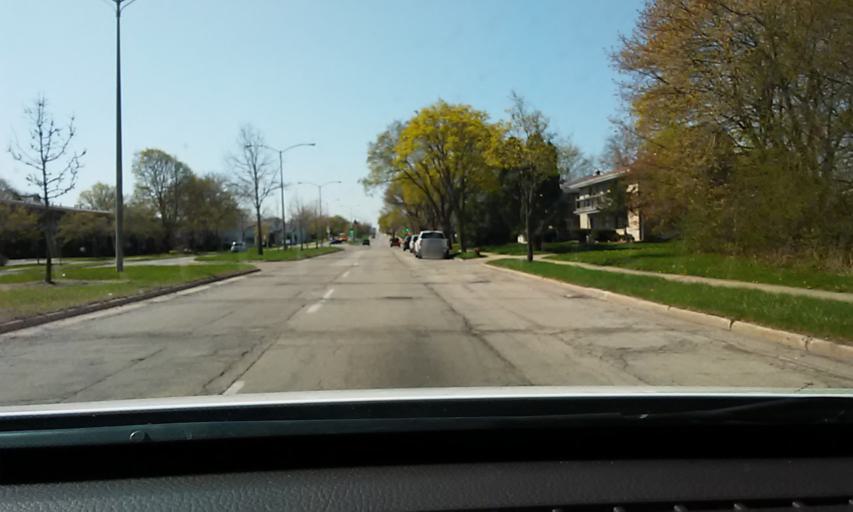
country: US
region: Wisconsin
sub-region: Milwaukee County
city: West Milwaukee
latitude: 42.9971
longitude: -87.9877
